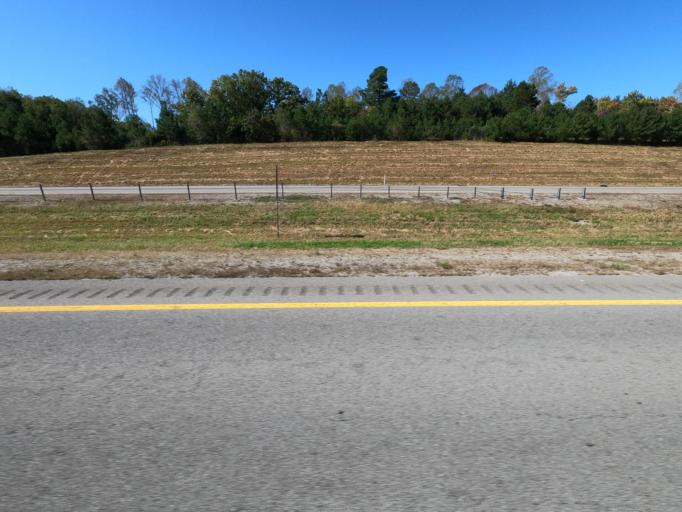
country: US
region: Tennessee
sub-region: Williamson County
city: Fairview
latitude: 35.8660
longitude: -87.0890
